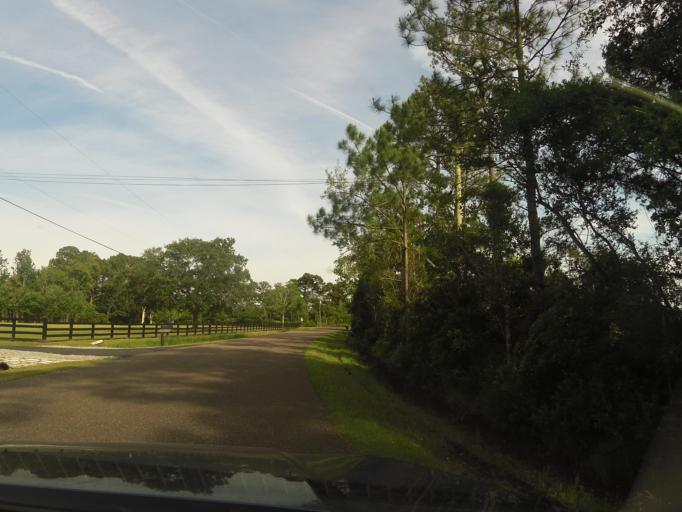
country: US
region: Florida
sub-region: Nassau County
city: Fernandina Beach
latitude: 30.5164
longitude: -81.4868
